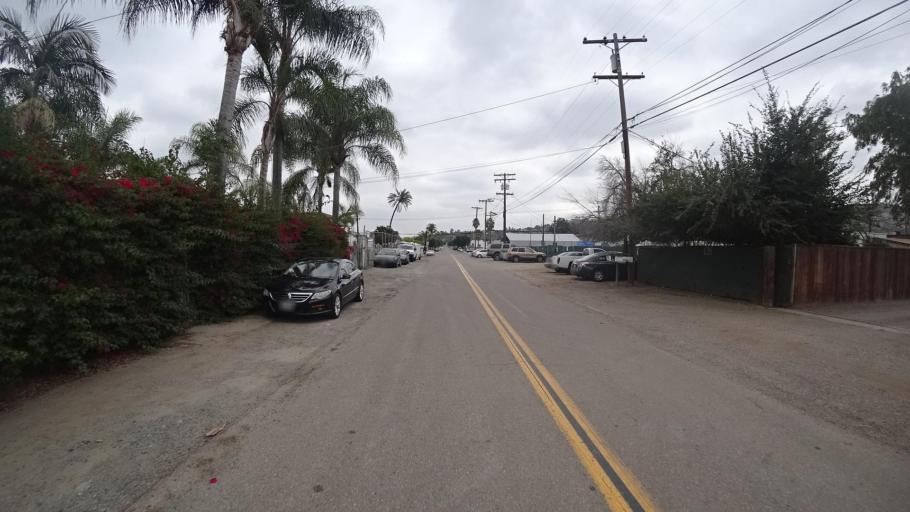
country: US
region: California
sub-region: San Diego County
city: Spring Valley
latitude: 32.7420
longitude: -117.0062
